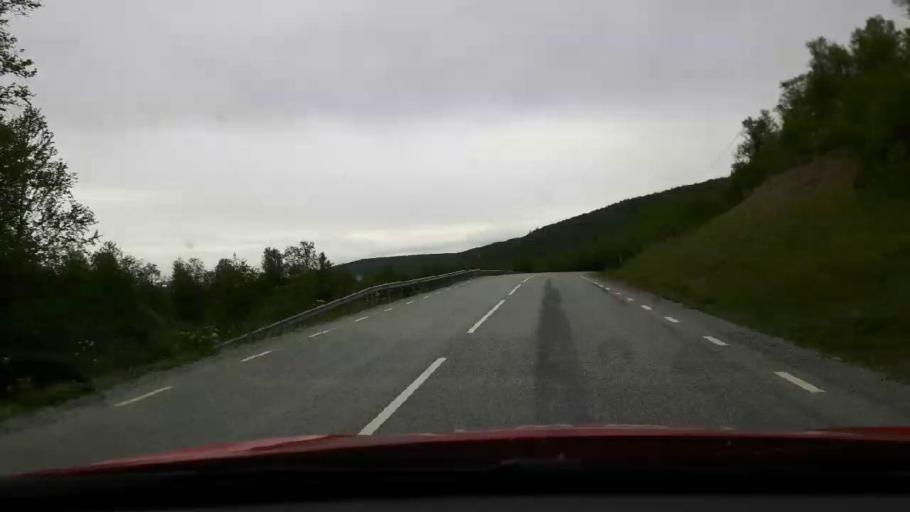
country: NO
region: Sor-Trondelag
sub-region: Tydal
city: Aas
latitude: 62.6698
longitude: 12.4298
